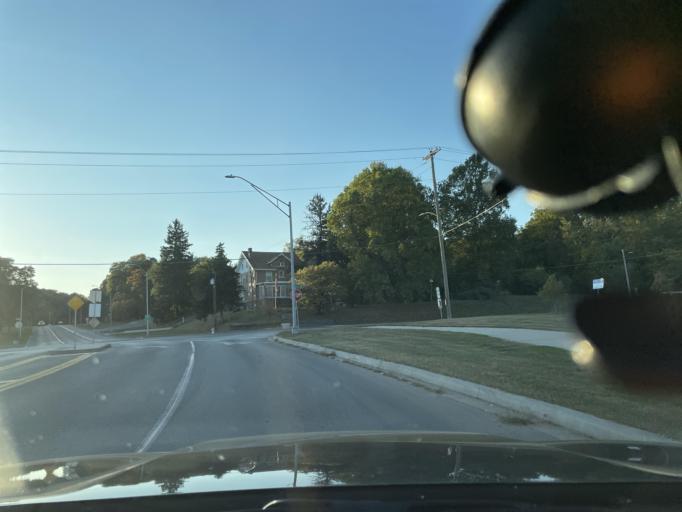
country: US
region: Missouri
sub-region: Buchanan County
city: Saint Joseph
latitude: 39.7991
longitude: -94.8443
